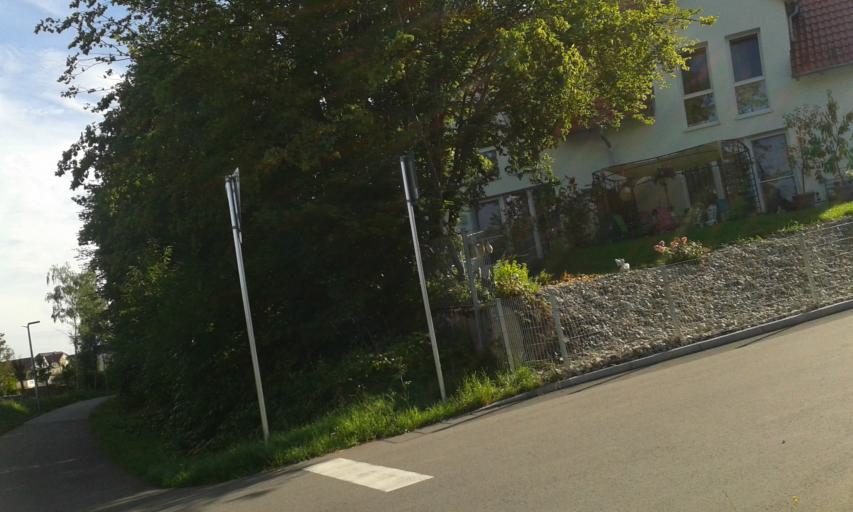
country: DE
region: Bavaria
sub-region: Upper Palatinate
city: Neustadt an der Waldnaab
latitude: 49.7269
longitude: 12.1688
